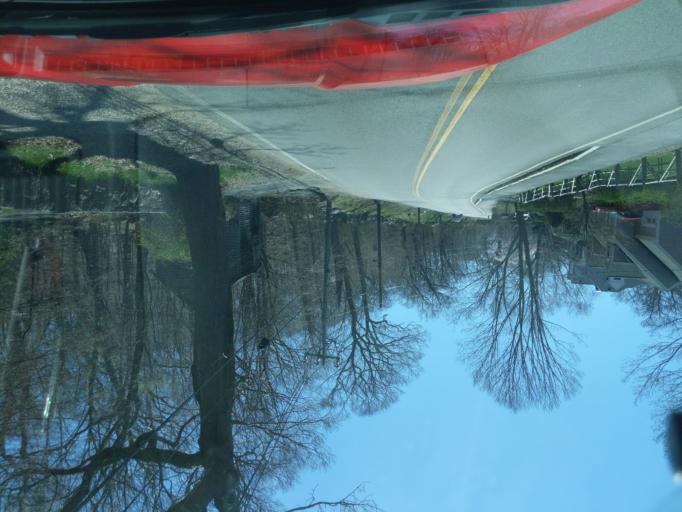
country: US
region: Massachusetts
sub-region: Essex County
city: Rockport
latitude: 42.6611
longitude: -70.6264
